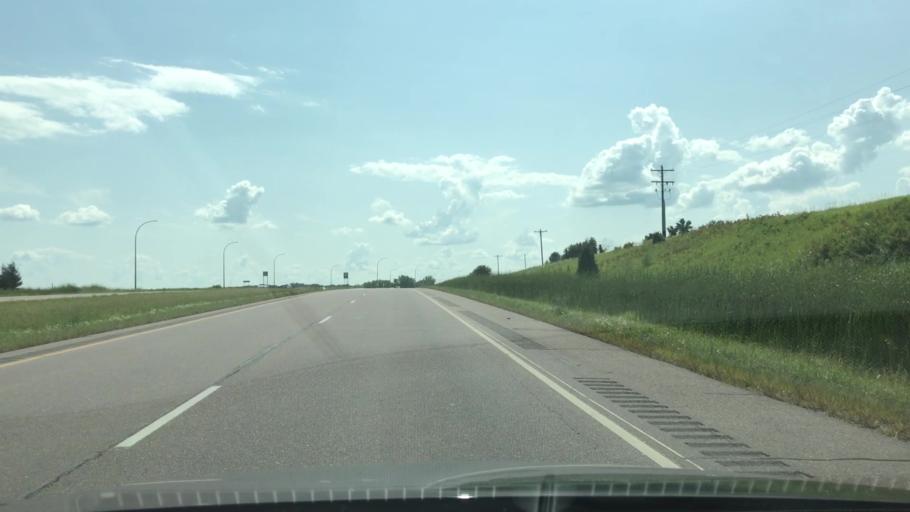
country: US
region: Minnesota
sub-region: Nicollet County
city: North Mankato
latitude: 44.1475
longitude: -94.0806
